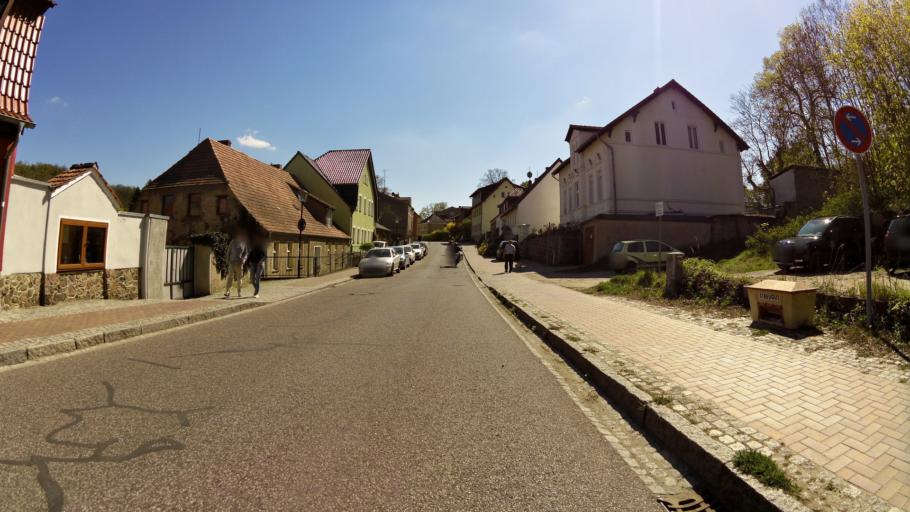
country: DE
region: Brandenburg
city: Buckow
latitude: 52.5654
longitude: 14.0743
